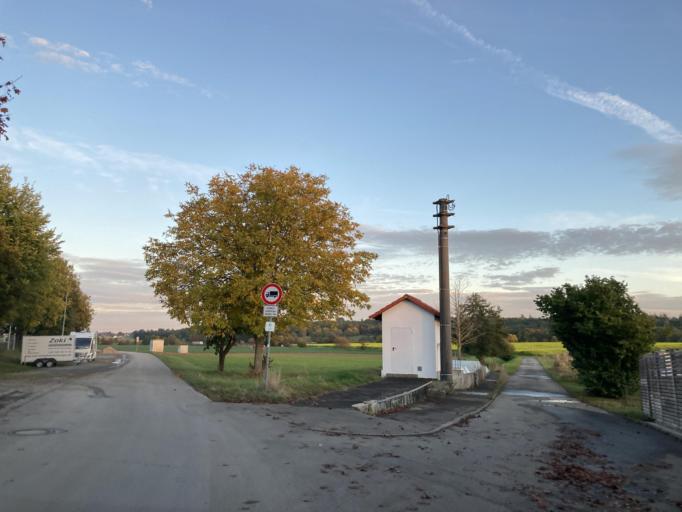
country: DE
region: Baden-Wuerttemberg
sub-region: Regierungsbezirk Stuttgart
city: Bondorf
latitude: 48.4897
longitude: 8.8166
